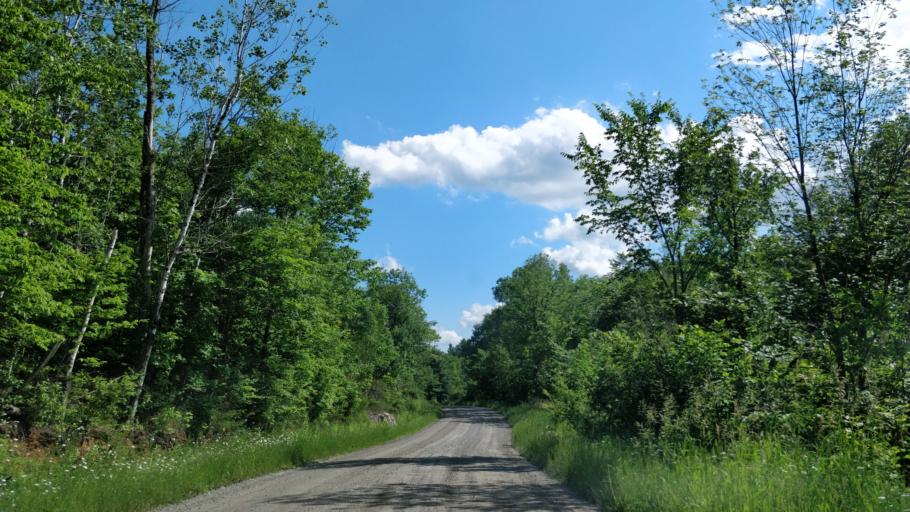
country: CA
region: Ontario
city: Perth
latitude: 44.6985
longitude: -76.5282
